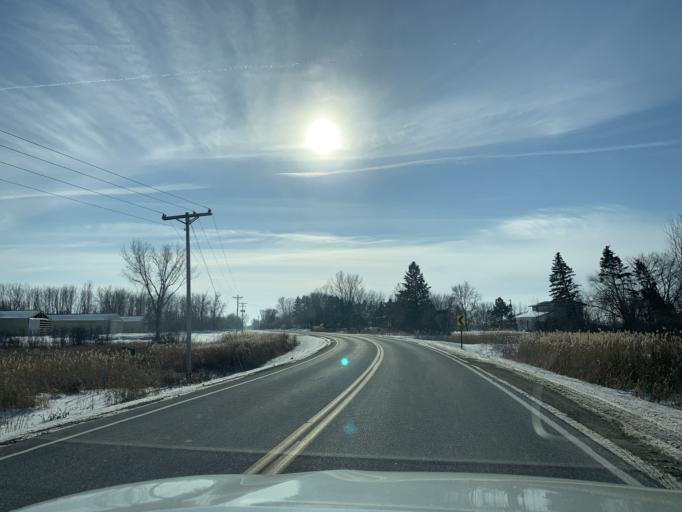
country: US
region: Minnesota
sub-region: Anoka County
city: Columbus
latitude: 45.2296
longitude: -93.0320
